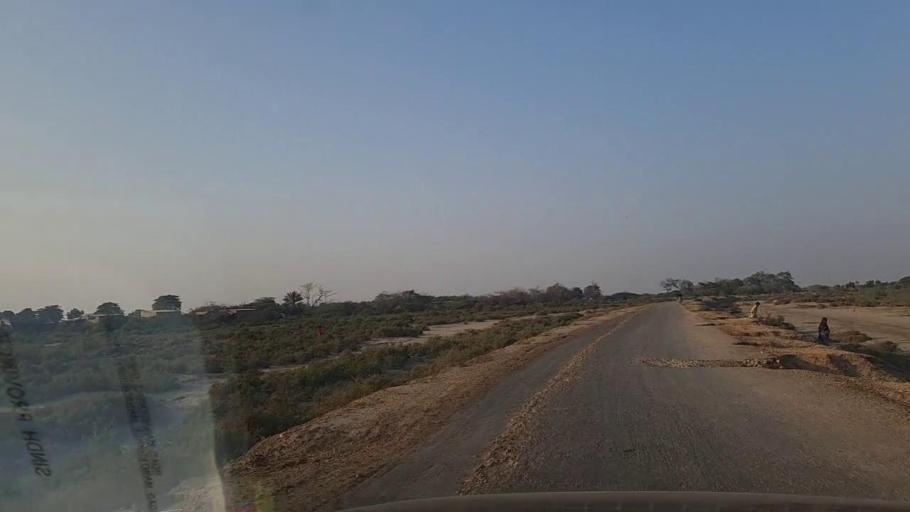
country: PK
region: Sindh
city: Keti Bandar
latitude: 24.2900
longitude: 67.5830
